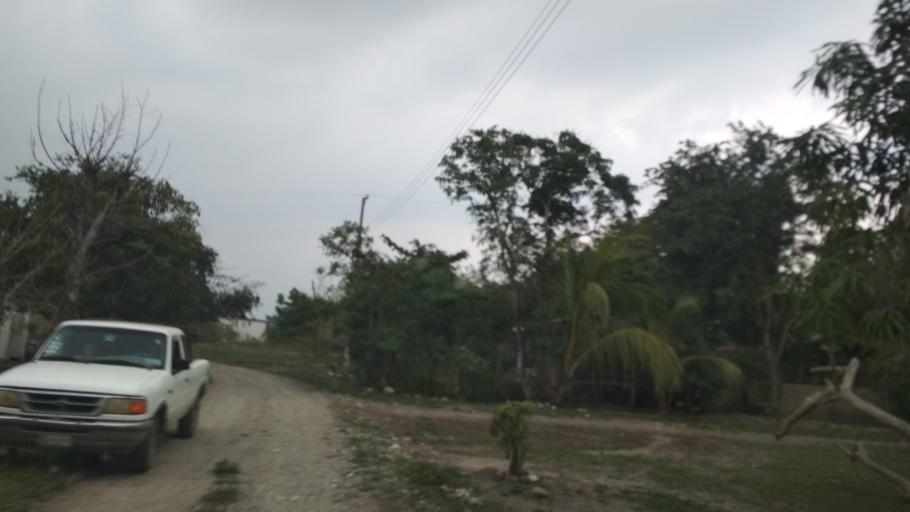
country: MM
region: Shan
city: Taunggyi
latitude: 20.3191
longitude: 97.3031
